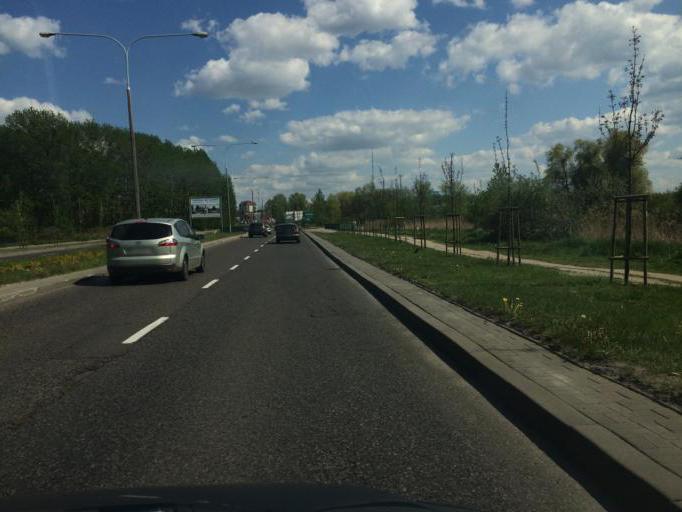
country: PL
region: Warmian-Masurian Voivodeship
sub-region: Olsztyn
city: Kortowo
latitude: 53.7658
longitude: 20.4752
